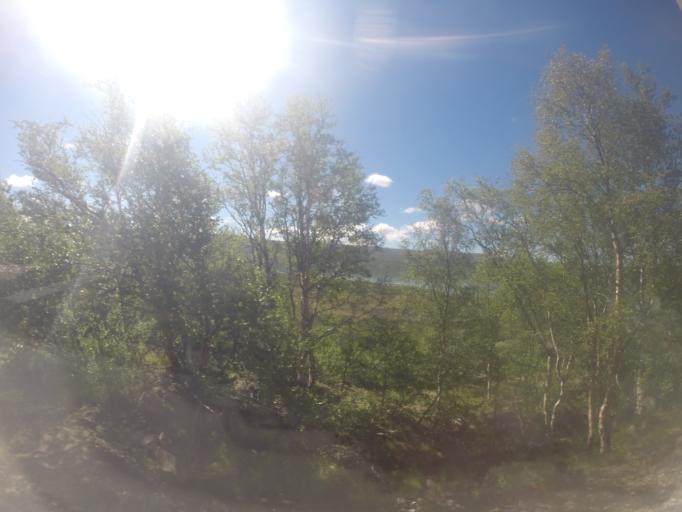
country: NO
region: Buskerud
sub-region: Hol
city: Geilo
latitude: 60.5005
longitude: 8.0203
